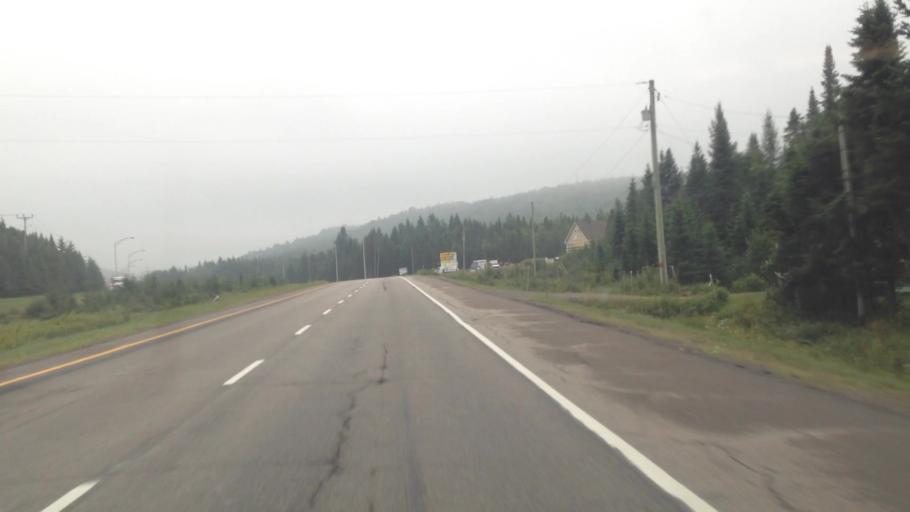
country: CA
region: Quebec
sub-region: Laurentides
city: Sainte-Agathe-des-Monts
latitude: 46.0999
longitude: -74.3759
